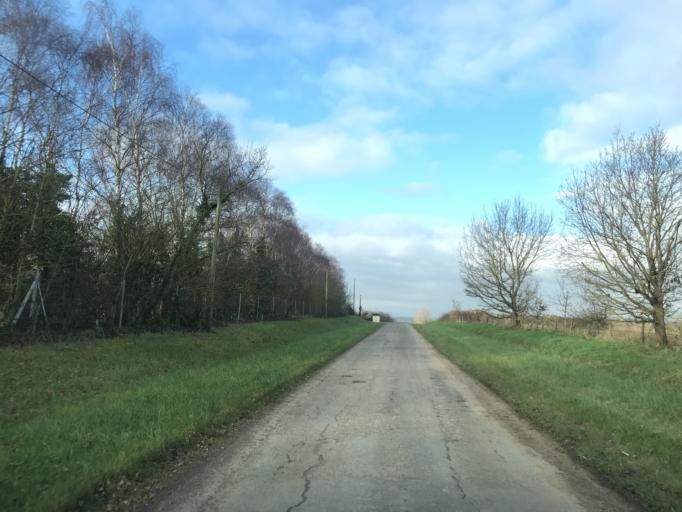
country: FR
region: Lower Normandy
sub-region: Departement du Calvados
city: Dives-sur-Mer
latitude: 49.2231
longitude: -0.1066
